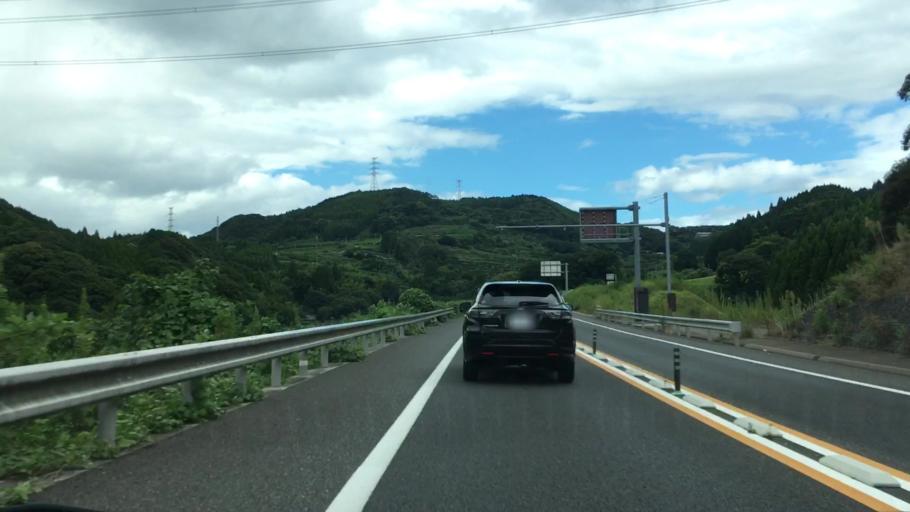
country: JP
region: Saga Prefecture
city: Karatsu
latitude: 33.3909
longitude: 129.9347
